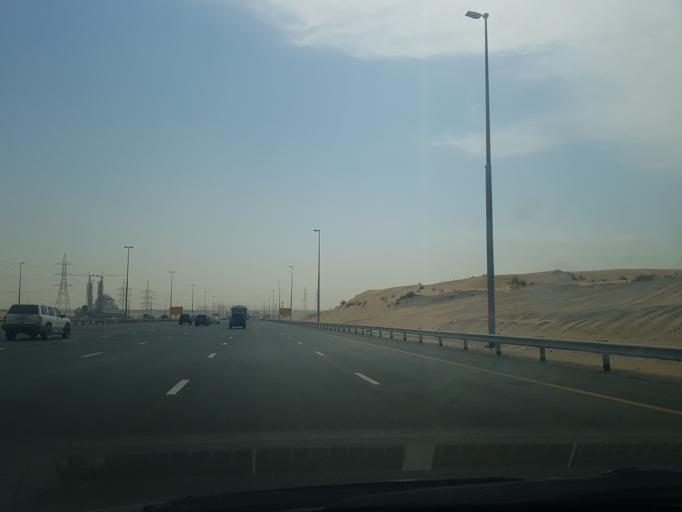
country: AE
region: Ash Shariqah
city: Sharjah
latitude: 25.2517
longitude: 55.5721
